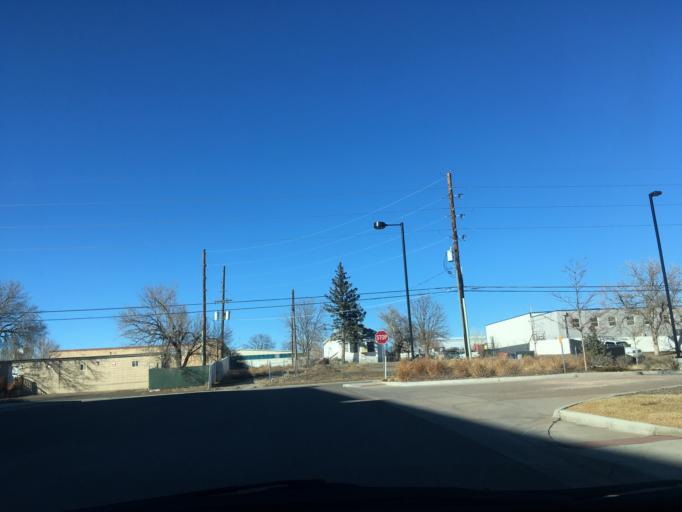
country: US
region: Colorado
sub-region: Adams County
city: Twin Lakes
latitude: 39.7961
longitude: -104.9840
